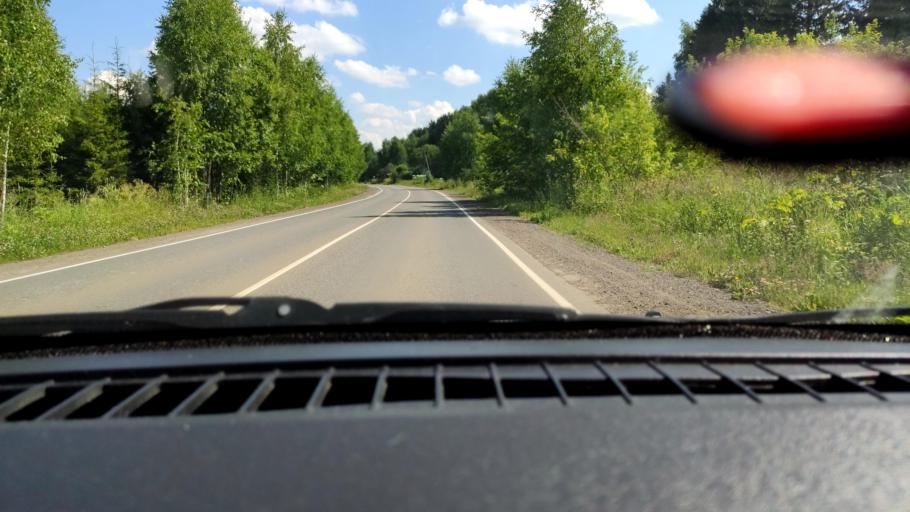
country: RU
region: Perm
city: Yugo-Kamskiy
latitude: 57.6836
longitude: 55.5371
